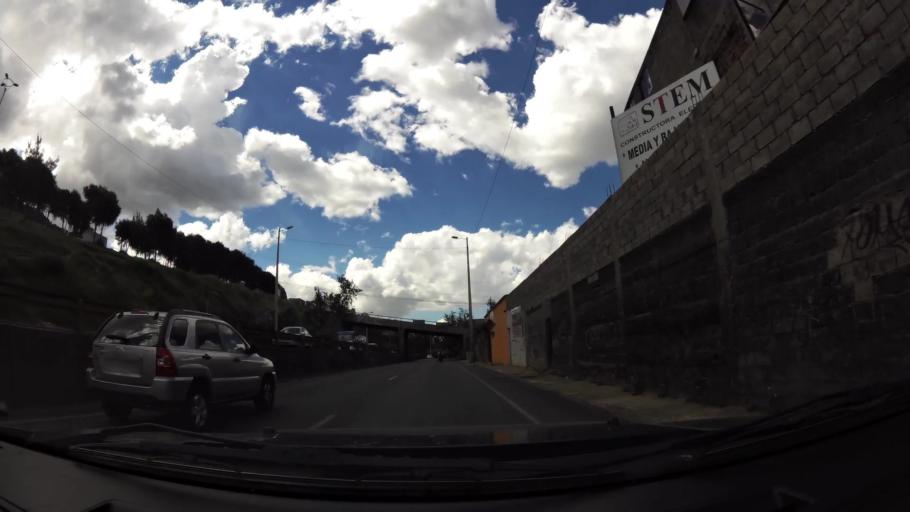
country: EC
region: Pichincha
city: Quito
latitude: -0.1846
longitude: -78.5097
